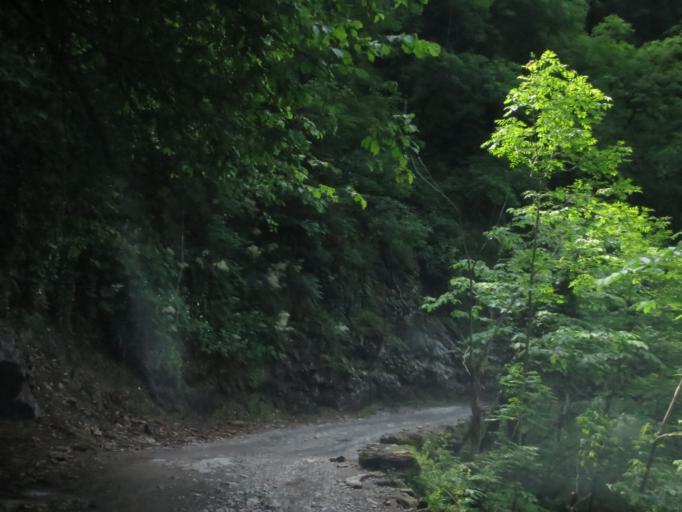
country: GE
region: Kakheti
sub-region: Telavi
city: Telavi
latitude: 42.2092
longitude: 45.4665
